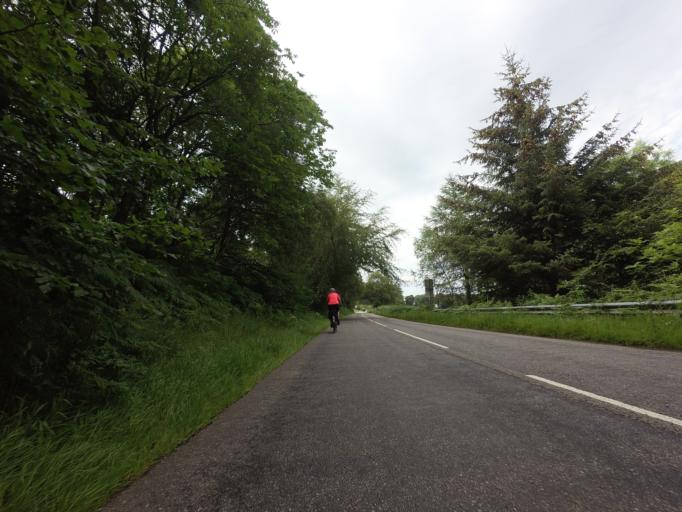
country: GB
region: Scotland
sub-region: Highland
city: Alness
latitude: 57.8526
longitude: -4.3010
